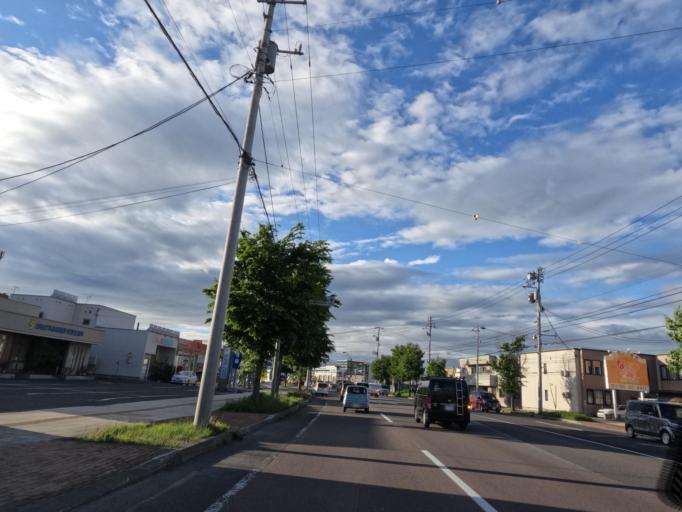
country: JP
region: Hokkaido
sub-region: Asahikawa-shi
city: Asahikawa
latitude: 43.7472
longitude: 142.3579
